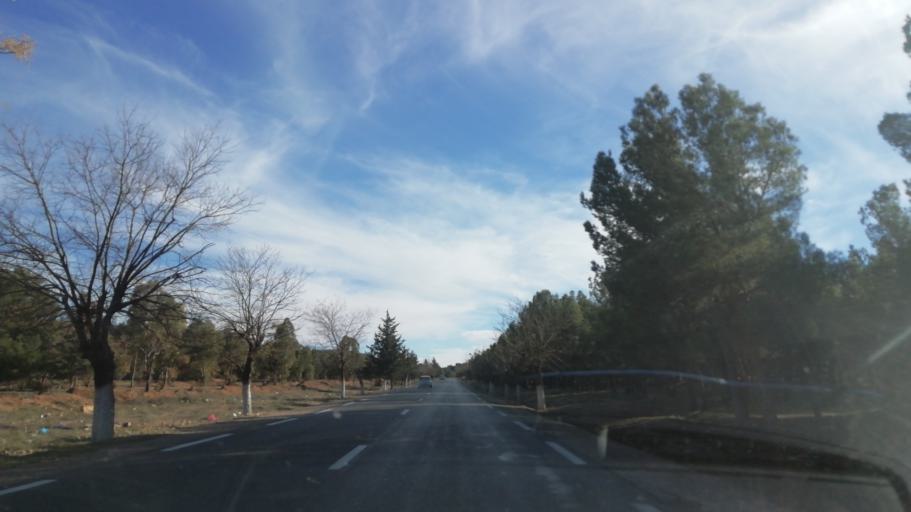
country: DZ
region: Tlemcen
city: Sebdou
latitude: 34.6174
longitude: -1.3340
